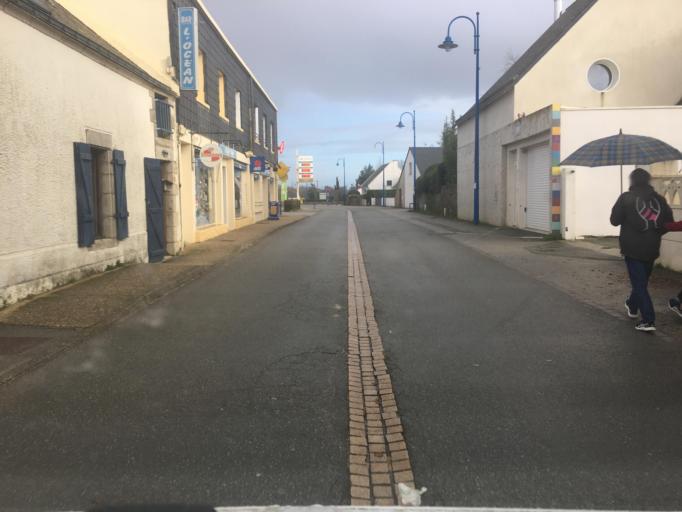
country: FR
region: Brittany
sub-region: Departement du Morbihan
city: Surzur
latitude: 47.5260
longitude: -2.6470
